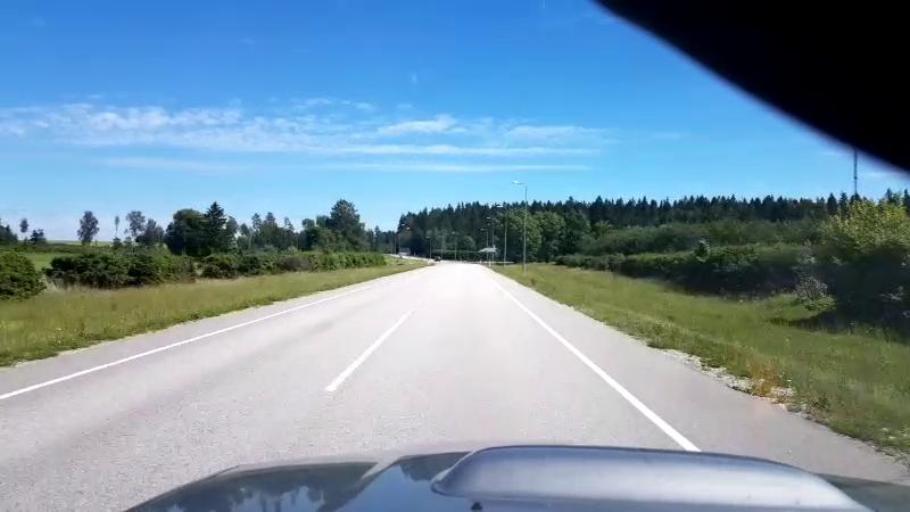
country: EE
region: Jaervamaa
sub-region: Koeru vald
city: Koeru
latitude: 58.9826
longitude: 26.0445
